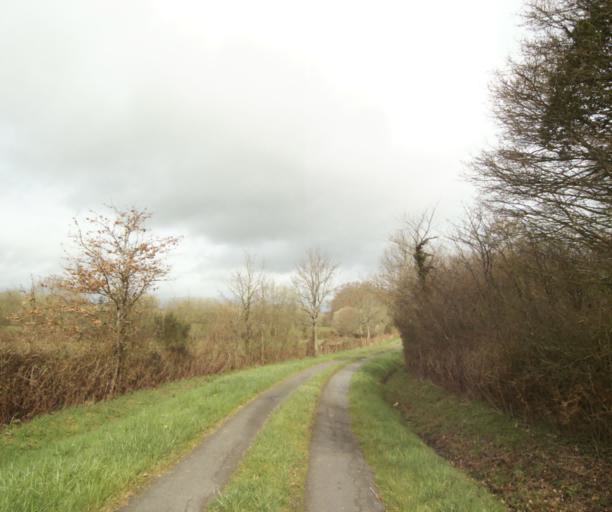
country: FR
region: Pays de la Loire
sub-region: Departement de la Loire-Atlantique
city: Bouvron
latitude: 47.4290
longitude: -1.8925
